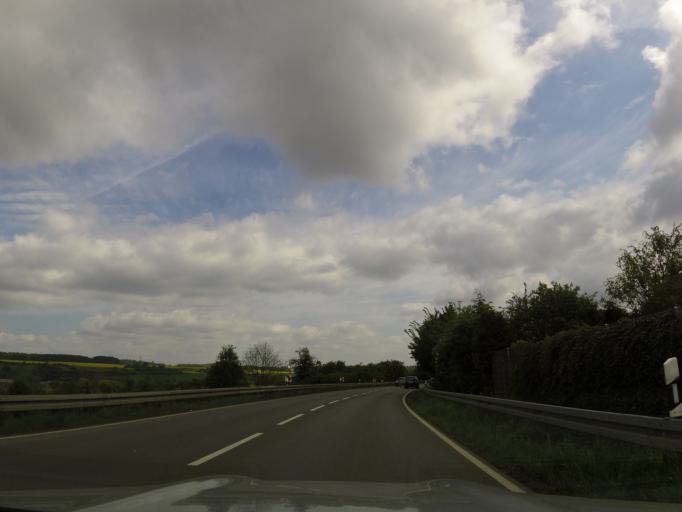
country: DE
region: Hesse
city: Albshausen
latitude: 50.5481
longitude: 8.4523
